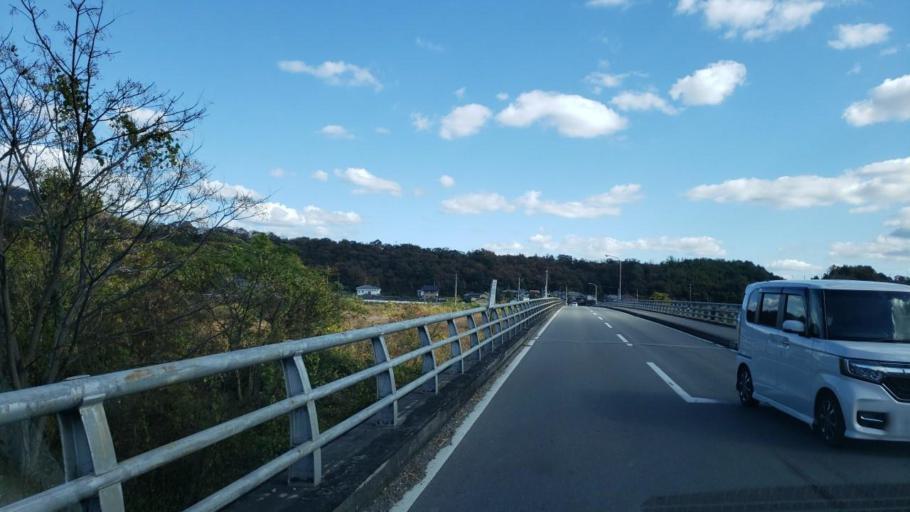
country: JP
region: Tokushima
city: Wakimachi
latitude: 34.0781
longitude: 134.1729
